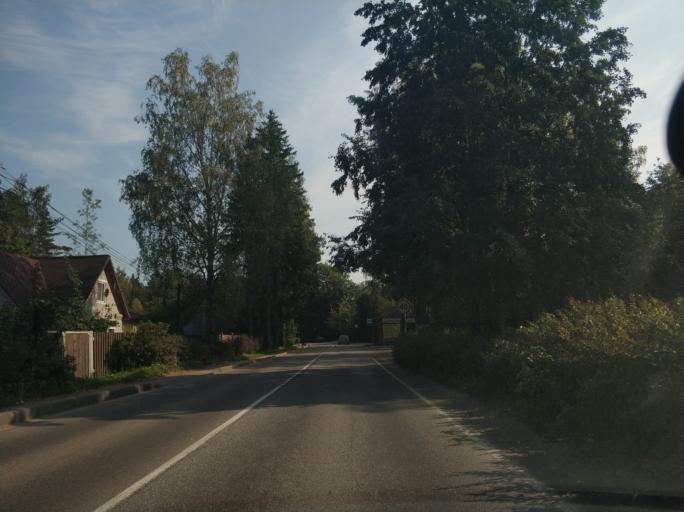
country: RU
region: Leningrad
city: Vsevolozhsk
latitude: 60.0088
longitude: 30.6002
